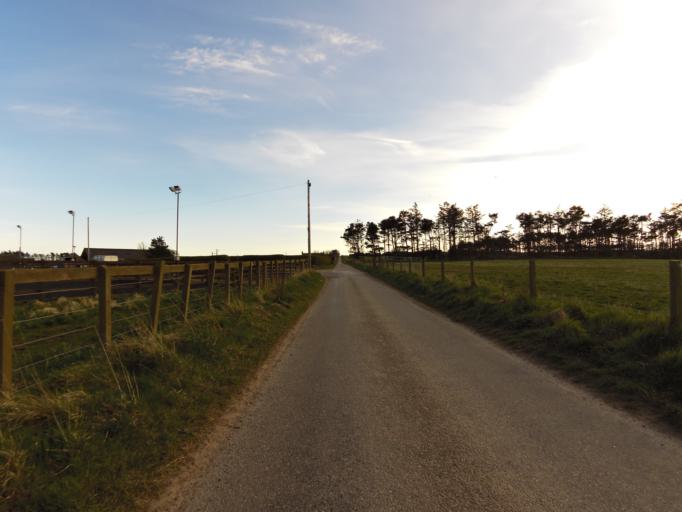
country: GB
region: Scotland
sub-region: Aberdeenshire
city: Stonehaven
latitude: 56.9440
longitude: -2.2202
